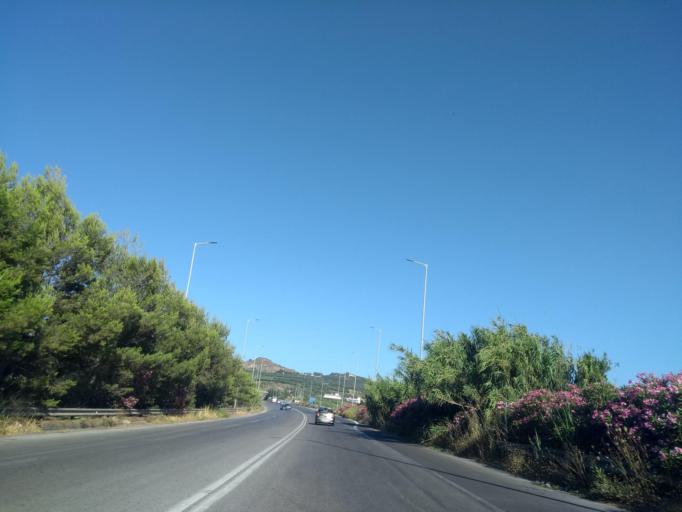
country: GR
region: Crete
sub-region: Nomos Chanias
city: Kolympari
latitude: 35.5293
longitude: 23.7902
